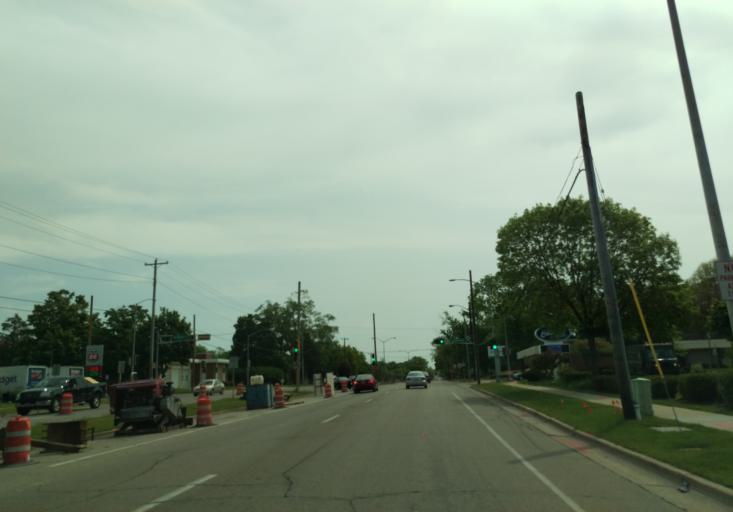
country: US
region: Wisconsin
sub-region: Dane County
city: Monona
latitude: 43.0840
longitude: -89.3078
